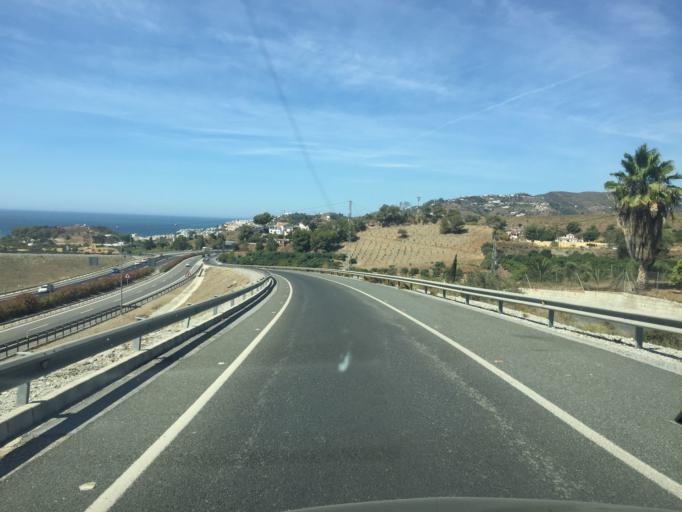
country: ES
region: Andalusia
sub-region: Provincia de Malaga
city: Nerja
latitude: 36.7631
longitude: -3.8891
